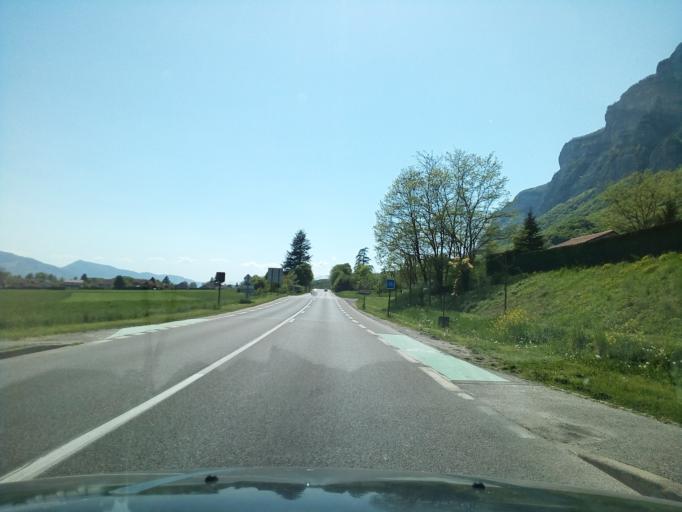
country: FR
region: Rhone-Alpes
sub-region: Departement de l'Isere
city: Lumbin
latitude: 45.3031
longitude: 5.9050
